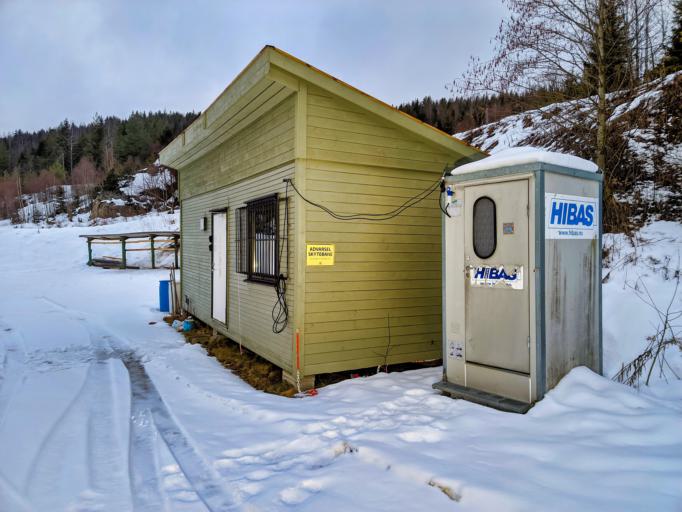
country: NO
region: Akershus
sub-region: Gjerdrum
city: Ask
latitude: 60.0498
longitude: 11.0165
